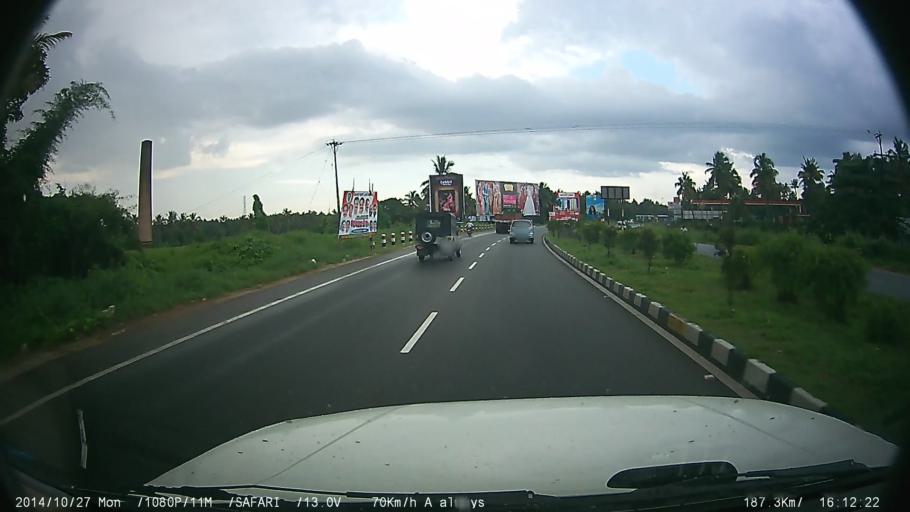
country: IN
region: Kerala
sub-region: Thrissur District
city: Irinjalakuda
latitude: 10.4056
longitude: 76.2763
